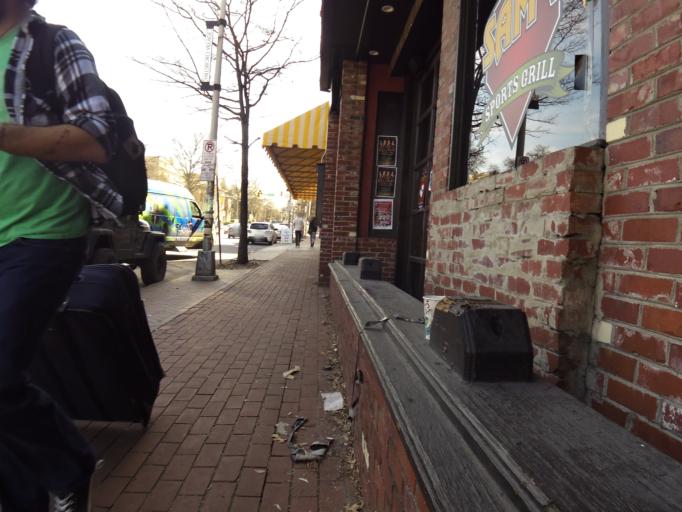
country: US
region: Tennessee
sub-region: Davidson County
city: Nashville
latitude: 36.1364
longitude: -86.8011
